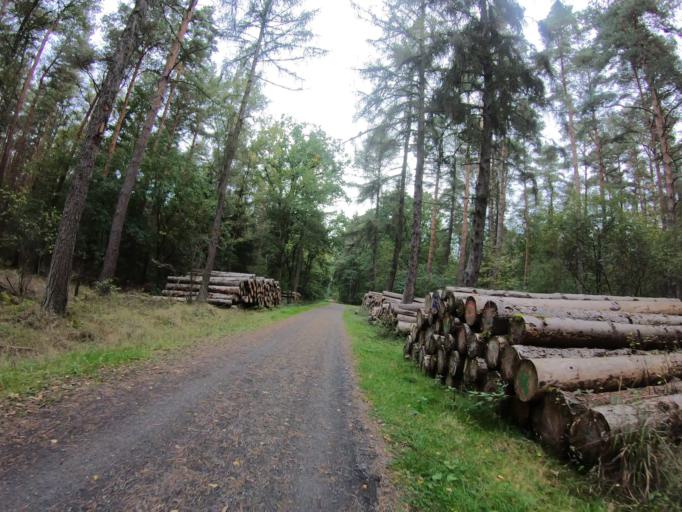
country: DE
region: Lower Saxony
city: Gifhorn
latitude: 52.4593
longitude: 10.5605
